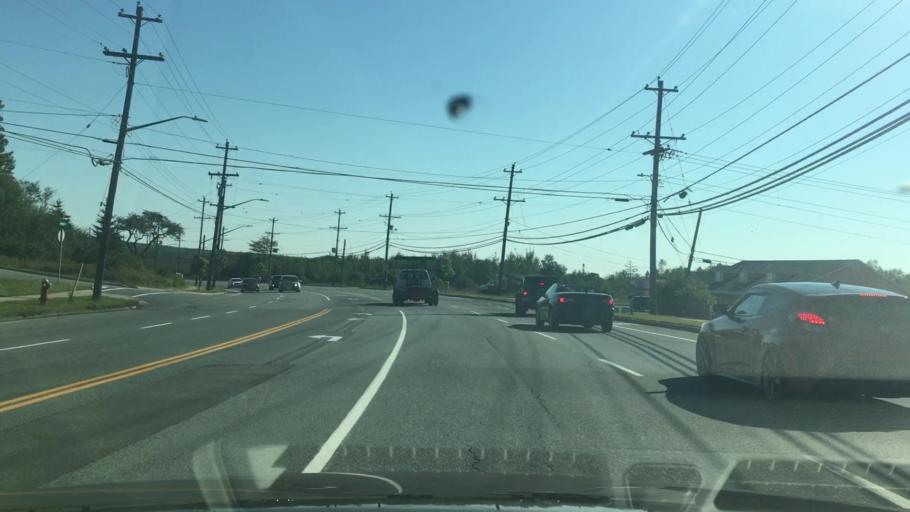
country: CA
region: Nova Scotia
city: Cole Harbour
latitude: 44.6983
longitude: -63.4872
